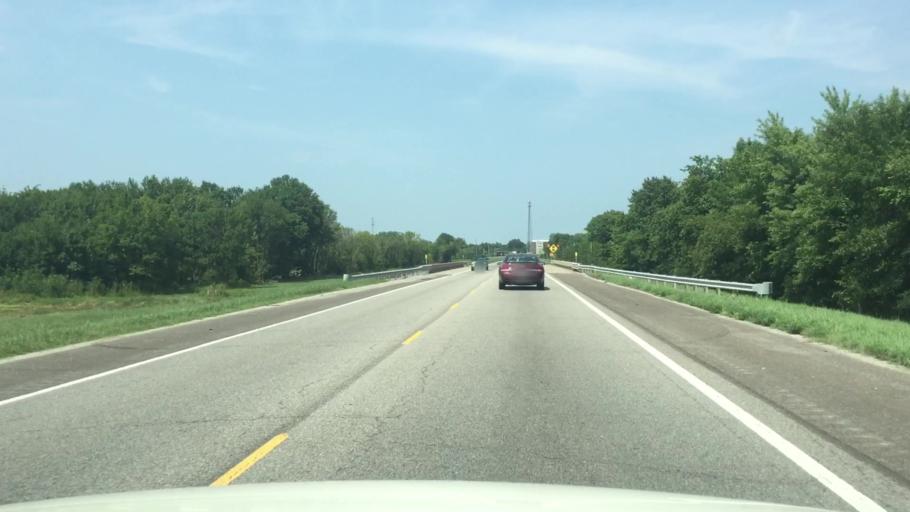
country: US
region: Kansas
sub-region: Crawford County
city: Pittsburg
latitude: 37.3730
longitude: -94.7084
